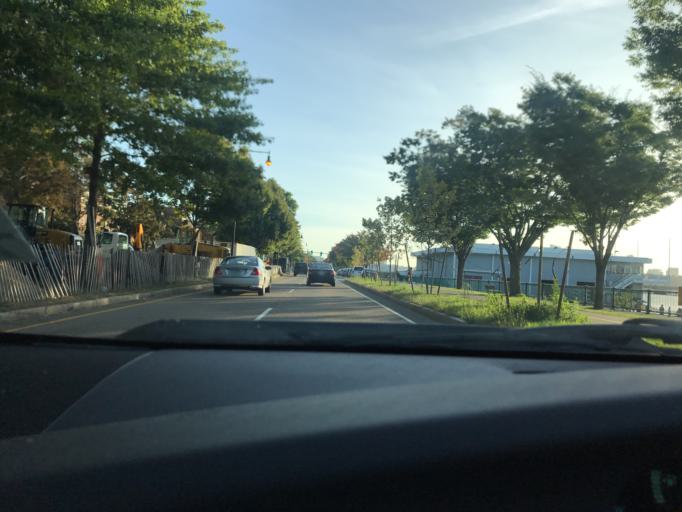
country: US
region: Massachusetts
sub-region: Middlesex County
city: Cambridge
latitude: 42.3552
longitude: -71.0984
